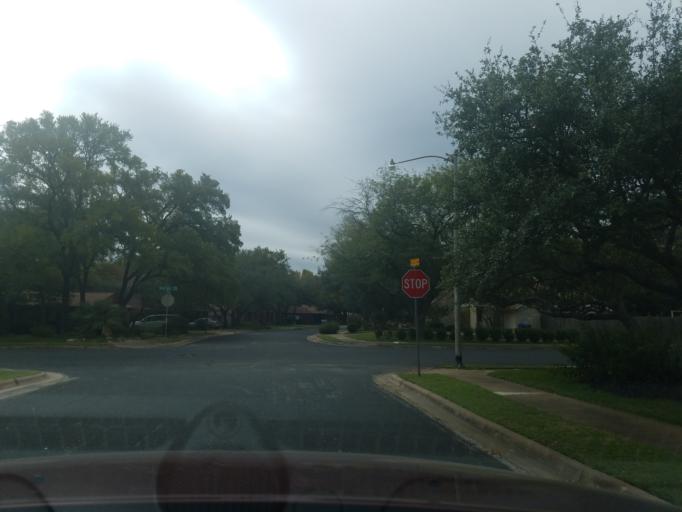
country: US
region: Texas
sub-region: Williamson County
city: Anderson Mill
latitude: 30.4635
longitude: -97.8072
